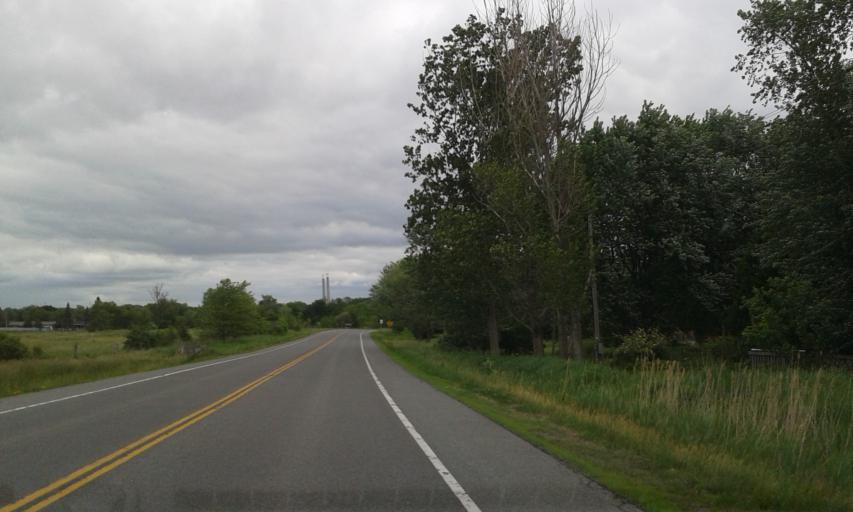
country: CA
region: Ontario
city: Napanee Downtown
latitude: 44.1253
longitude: -76.8920
